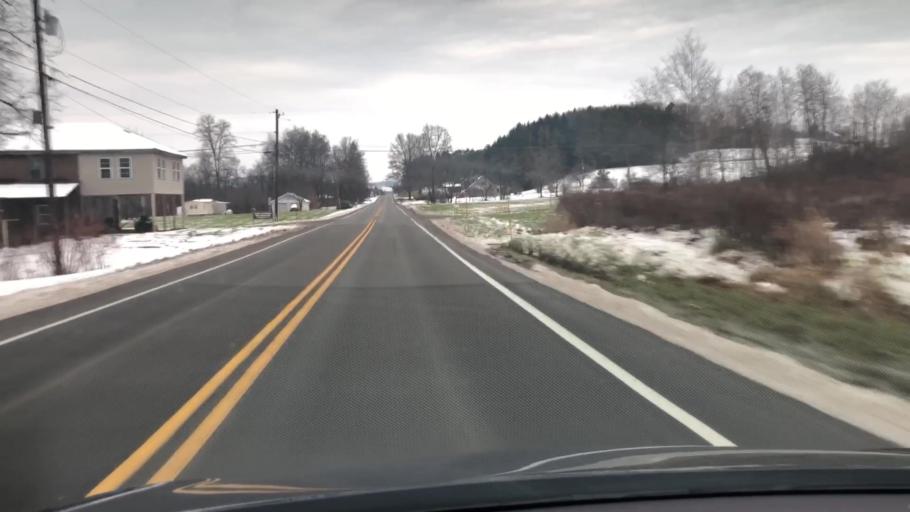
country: US
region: Pennsylvania
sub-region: Jefferson County
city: Brookville
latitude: 41.0805
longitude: -79.2330
